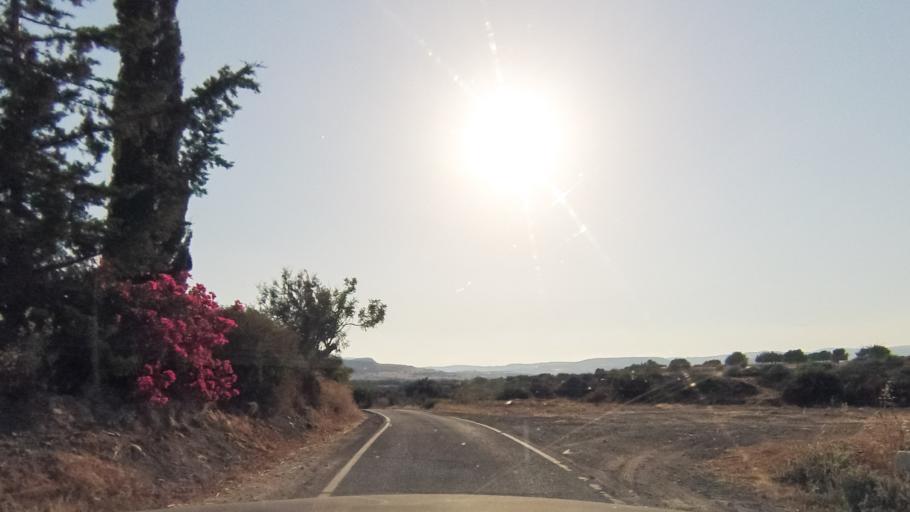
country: CY
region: Limassol
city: Pissouri
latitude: 34.6743
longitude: 32.7653
